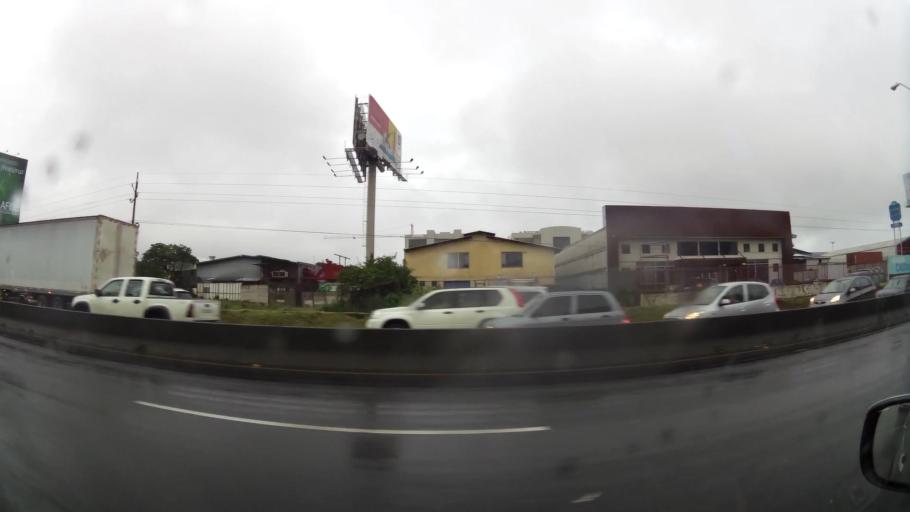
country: CR
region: Heredia
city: La Asuncion
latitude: 9.9885
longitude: -84.1652
